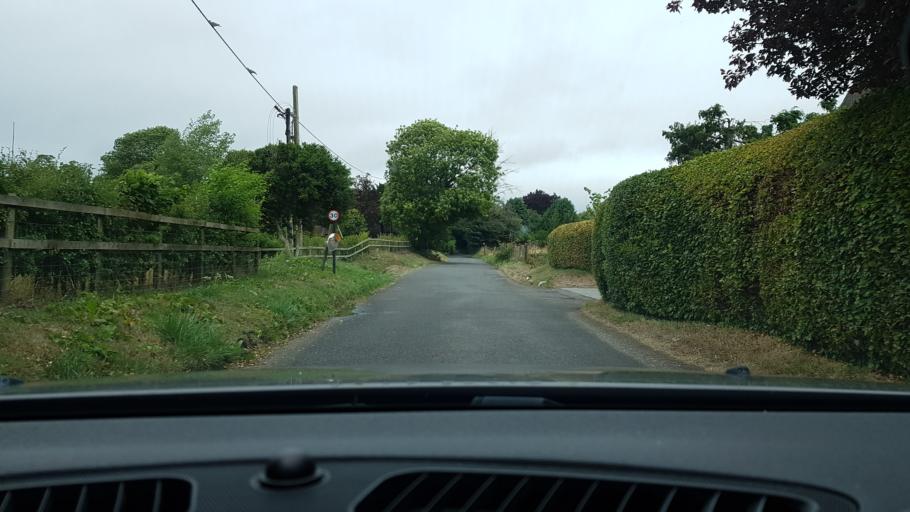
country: GB
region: England
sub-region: Wiltshire
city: Shalbourne
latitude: 51.3608
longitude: -1.5254
